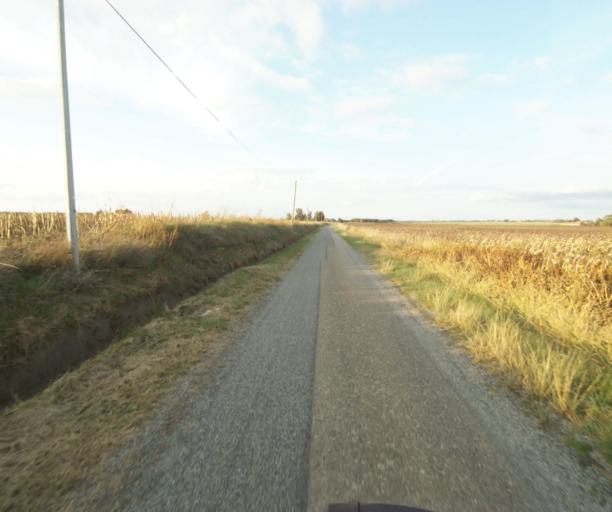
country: FR
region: Midi-Pyrenees
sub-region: Departement de la Haute-Garonne
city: Launac
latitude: 43.8079
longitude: 1.1634
